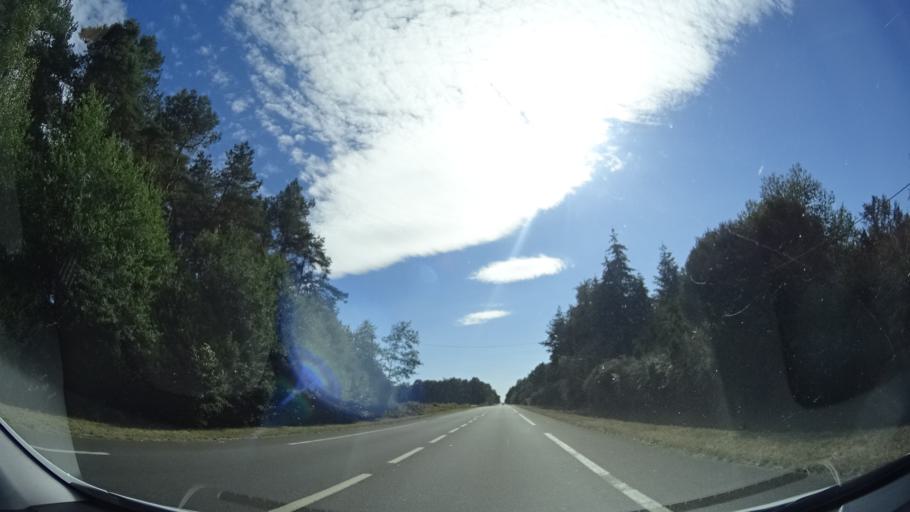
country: FR
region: Centre
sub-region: Departement du Loiret
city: Vitry-aux-Loges
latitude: 47.9342
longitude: 2.3452
